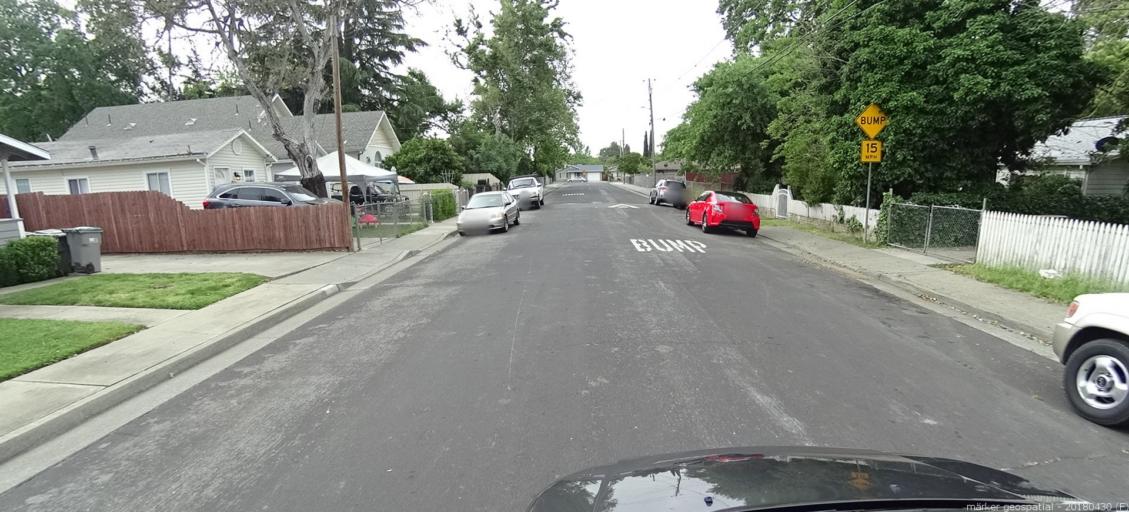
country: US
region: California
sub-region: Yolo County
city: West Sacramento
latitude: 38.5971
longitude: -121.5382
